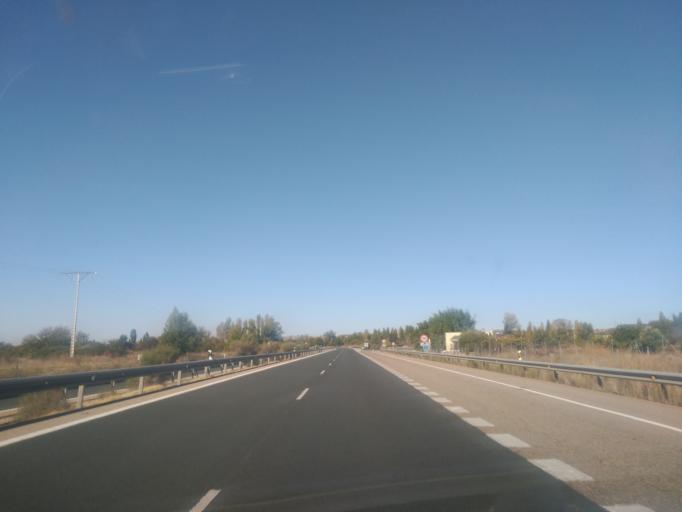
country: ES
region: Castille and Leon
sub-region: Provincia de Valladolid
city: Tudela de Duero
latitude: 41.5928
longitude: -4.5742
